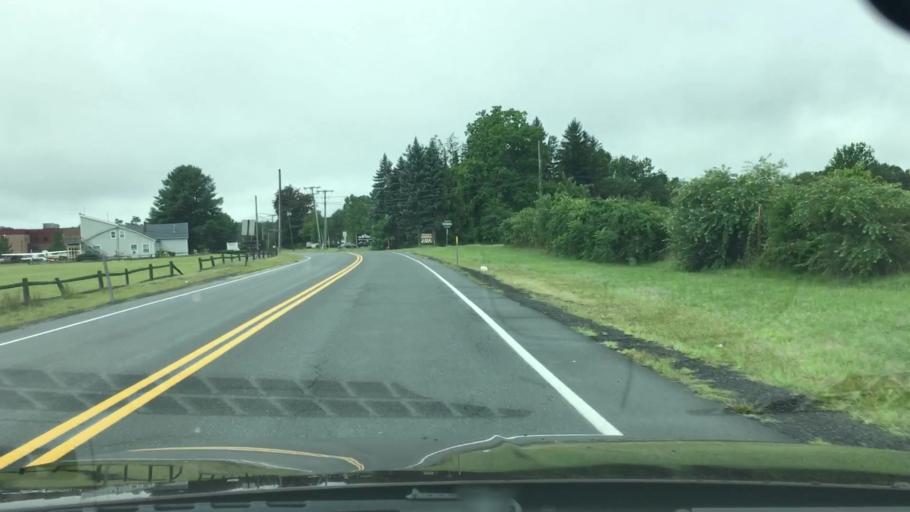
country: US
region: Connecticut
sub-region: Hartford County
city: Tariffville
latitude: 41.9183
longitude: -72.7775
